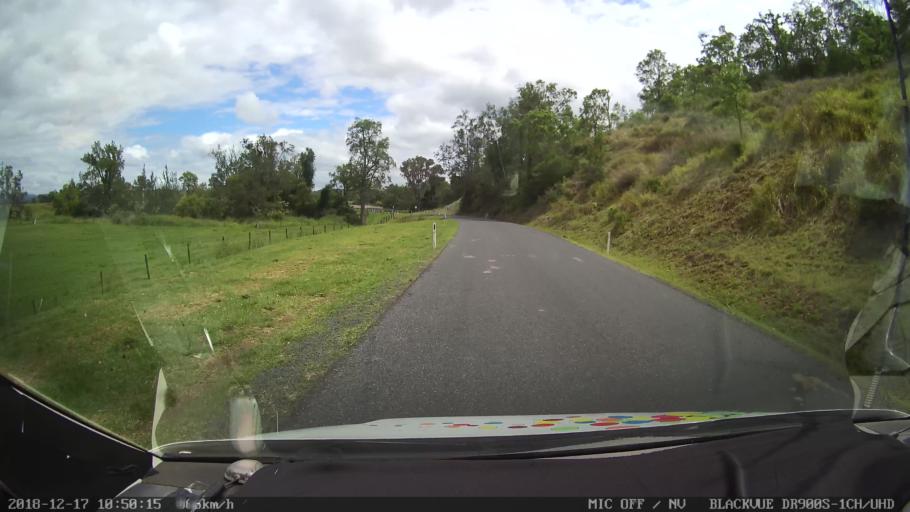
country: AU
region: New South Wales
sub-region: Clarence Valley
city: Gordon
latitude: -28.8608
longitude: 152.5742
